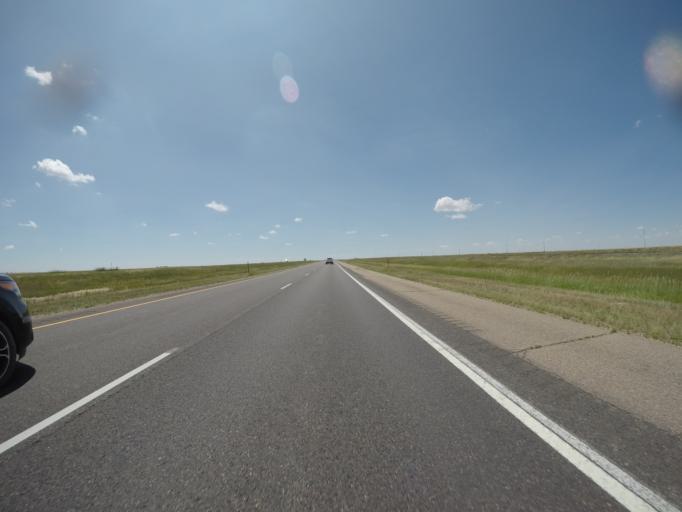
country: US
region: Colorado
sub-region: Lincoln County
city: Hugo
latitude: 39.2825
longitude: -103.3067
